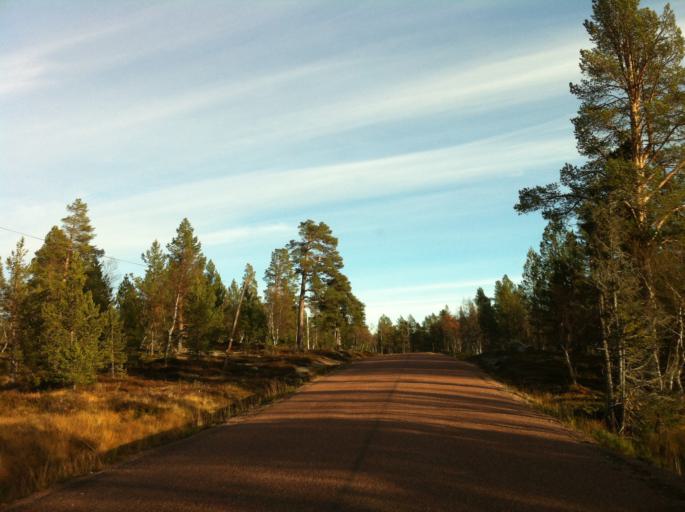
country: NO
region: Hedmark
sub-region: Engerdal
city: Engerdal
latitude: 62.0806
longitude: 12.1462
